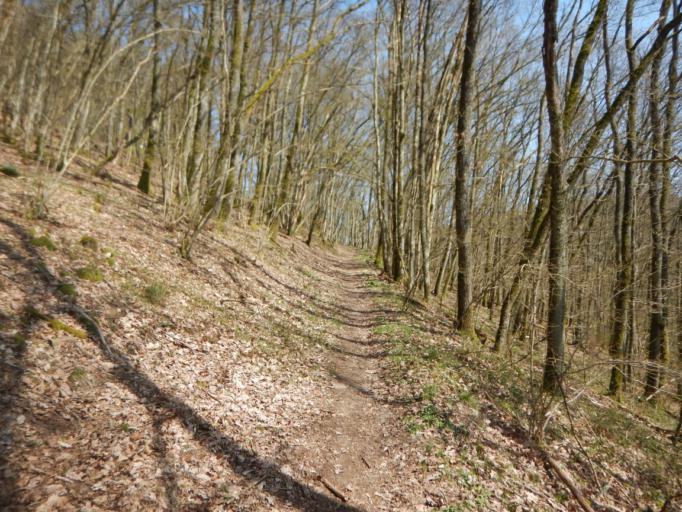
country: LU
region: Diekirch
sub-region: Canton de Diekirch
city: Bourscheid
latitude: 49.9367
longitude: 6.0724
